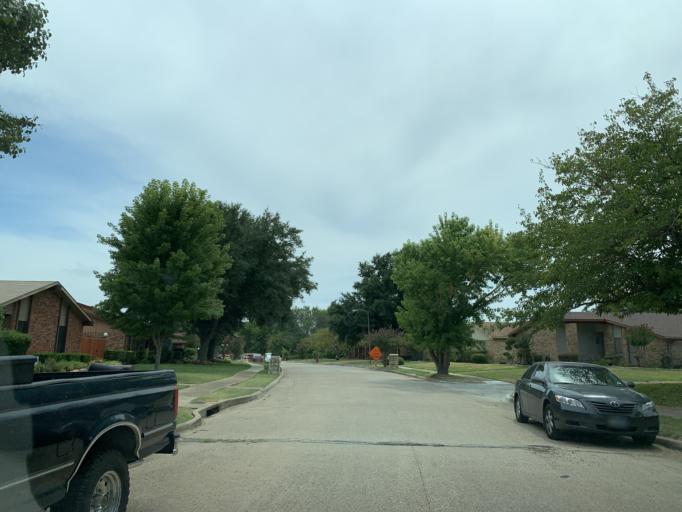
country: US
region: Texas
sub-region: Dallas County
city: Cedar Hill
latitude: 32.6520
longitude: -97.0305
